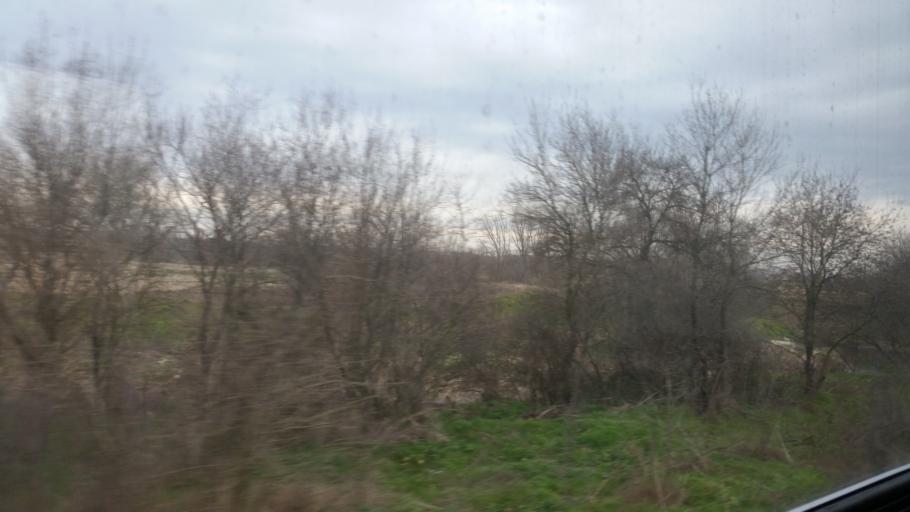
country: TR
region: Tekirdag
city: Velimese
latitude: 41.2376
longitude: 27.8718
